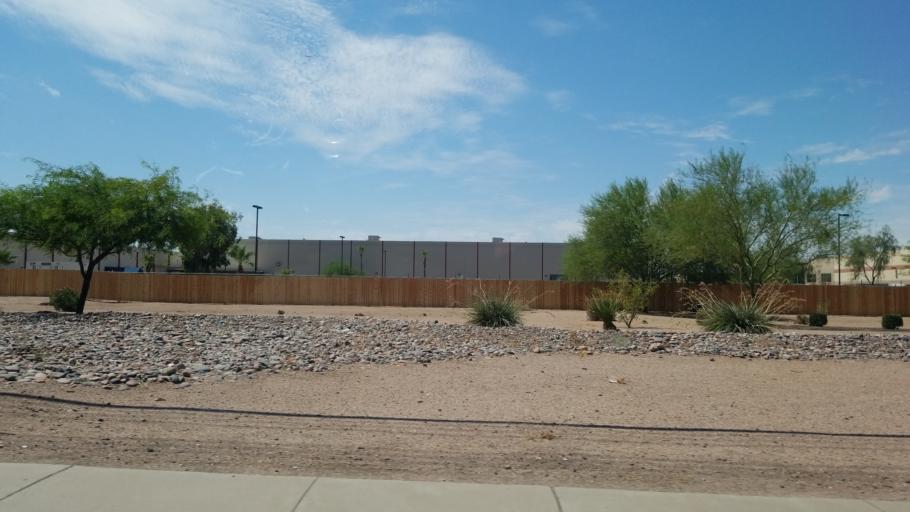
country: US
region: Arizona
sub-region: Maricopa County
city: Laveen
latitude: 33.4368
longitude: -112.1558
